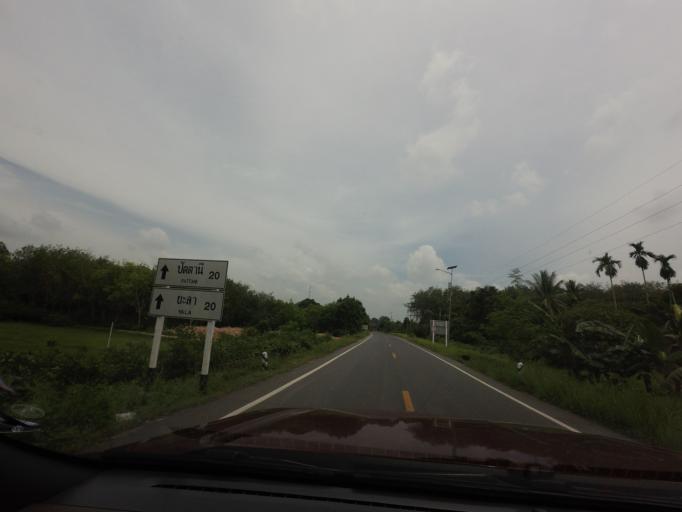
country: TH
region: Pattani
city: Yarang
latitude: 6.7136
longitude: 101.2957
